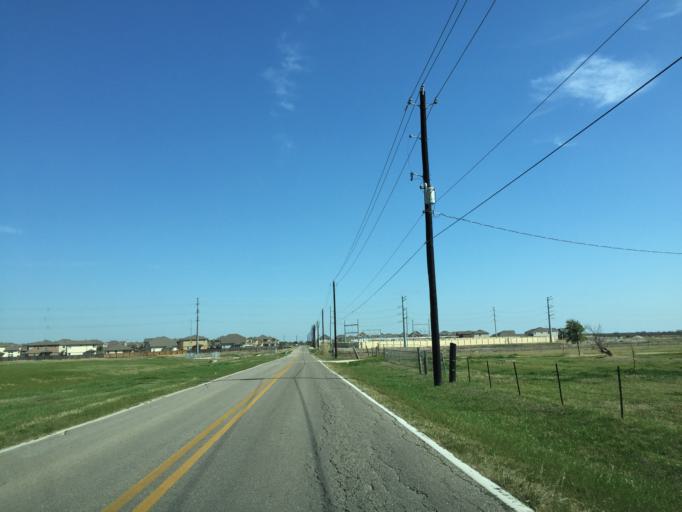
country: US
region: Texas
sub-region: Travis County
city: Garfield
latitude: 30.1564
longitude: -97.6382
